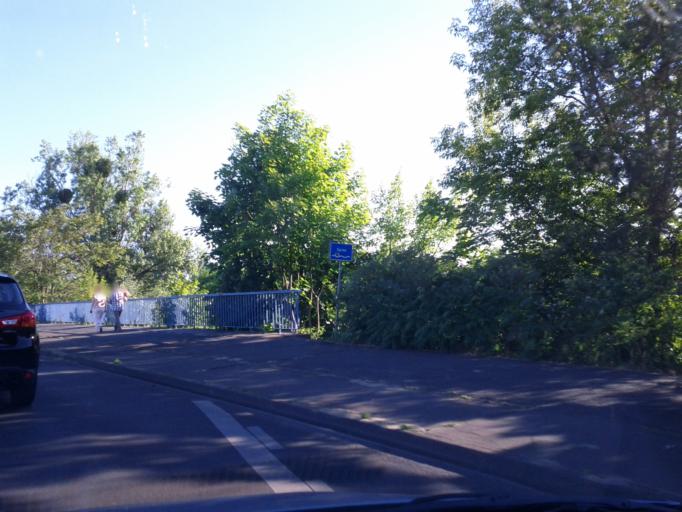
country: DE
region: Berlin
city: Berlin Koepenick
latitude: 52.4508
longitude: 13.5932
